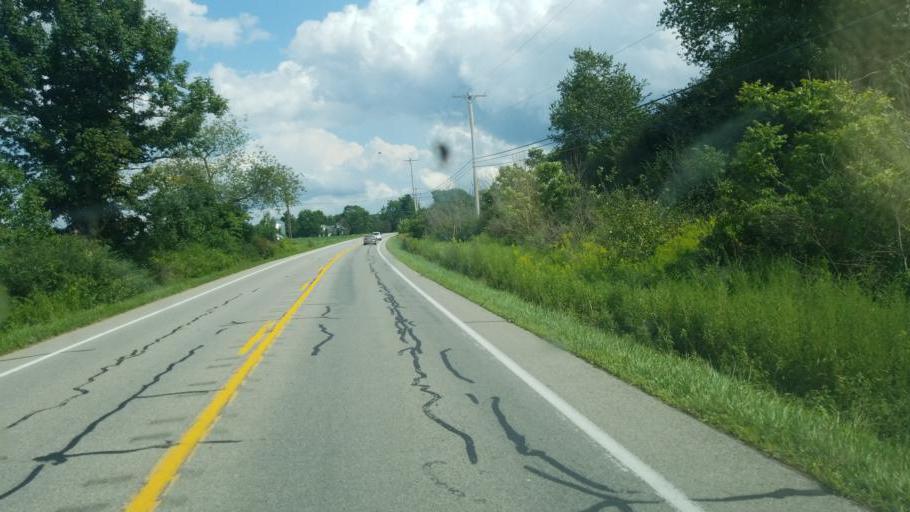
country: US
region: Pennsylvania
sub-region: Crawford County
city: Pymatuning Central
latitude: 41.6059
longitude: -80.4777
